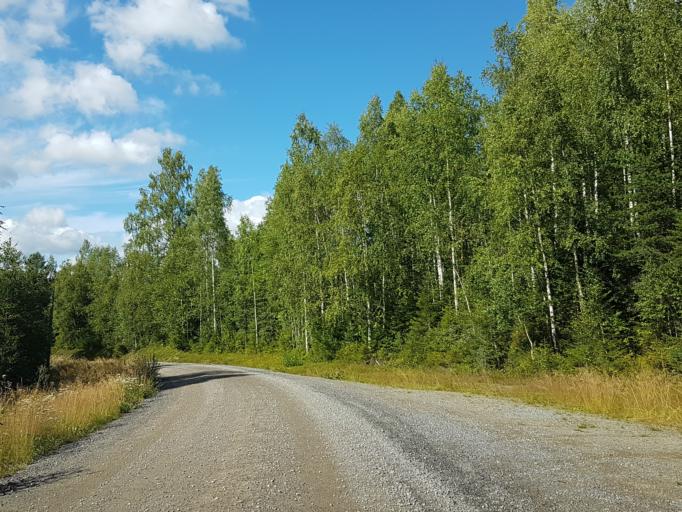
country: SE
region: Vaesterbotten
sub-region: Skelleftea Kommun
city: Burtraesk
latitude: 64.2777
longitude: 20.4798
